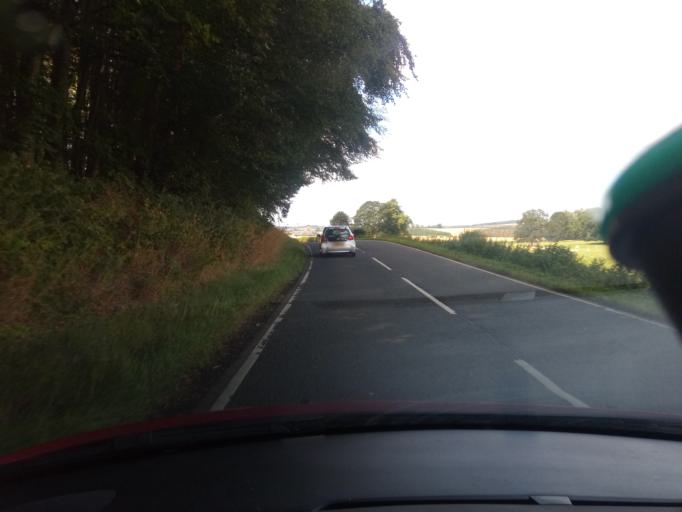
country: GB
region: Scotland
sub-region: The Scottish Borders
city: Jedburgh
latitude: 55.5731
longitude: -2.5482
